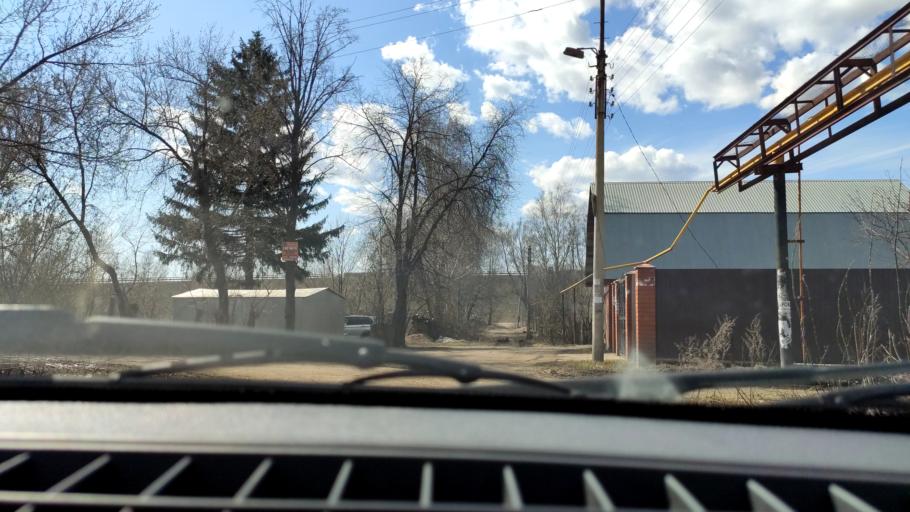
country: RU
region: Bashkortostan
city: Avdon
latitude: 54.6775
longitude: 55.8155
